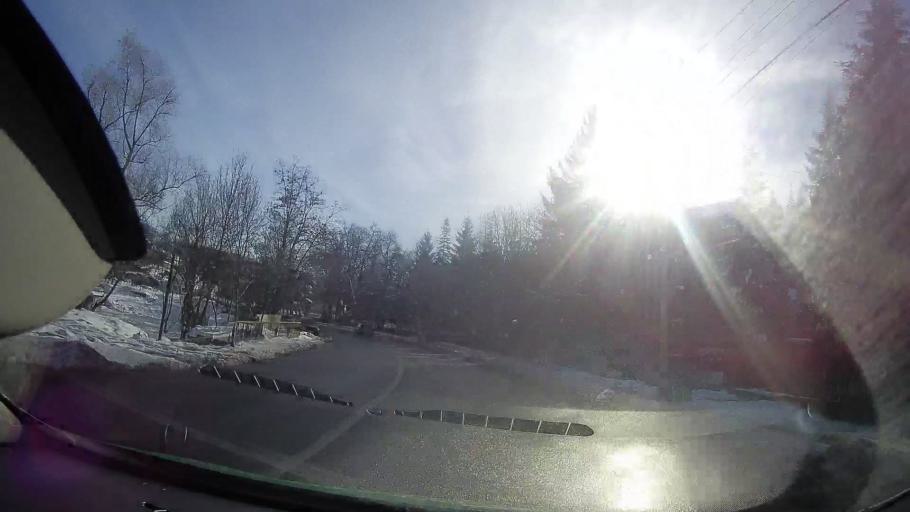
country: RO
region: Neamt
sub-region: Comuna Baltatesti
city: Baltatesti
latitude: 47.1206
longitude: 26.3096
